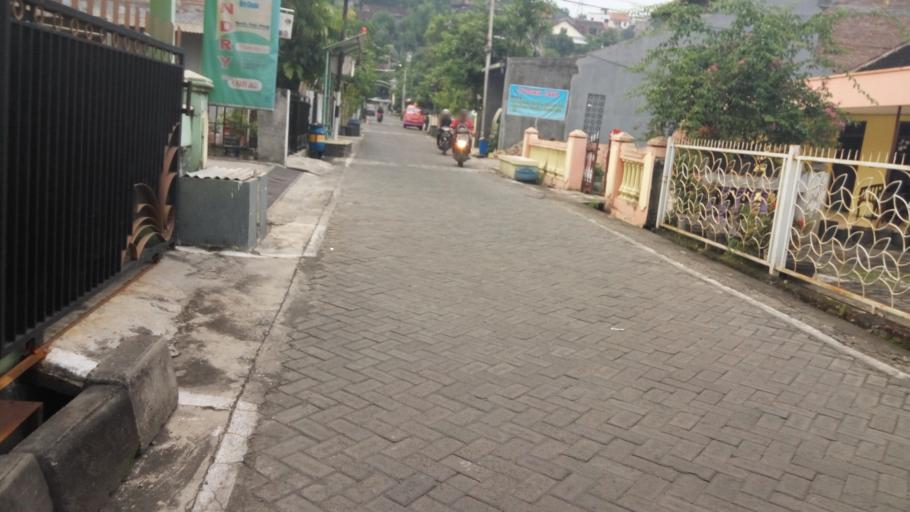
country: ID
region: Central Java
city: Semarang
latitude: -7.0166
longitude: 110.3854
